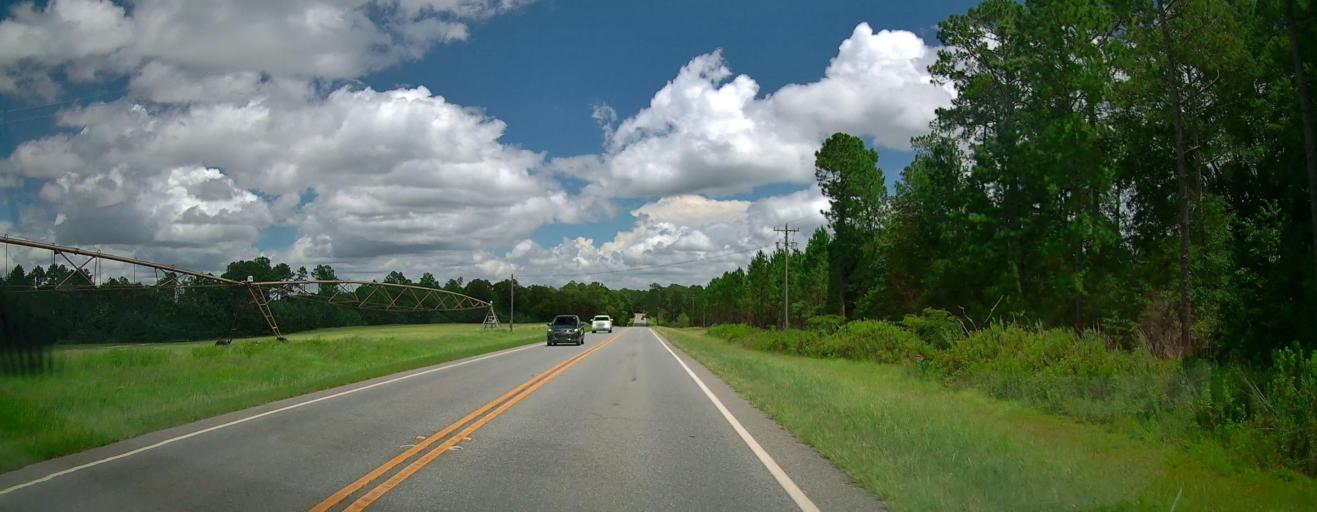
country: US
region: Georgia
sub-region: Turner County
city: Ashburn
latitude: 31.7206
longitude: -83.5929
